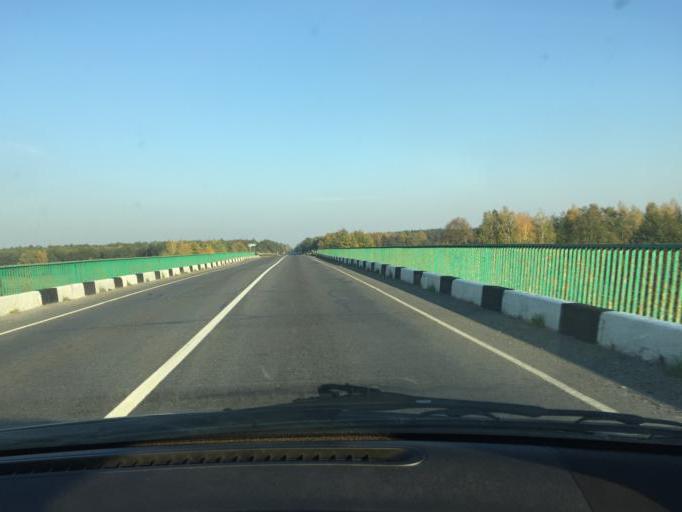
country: BY
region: Brest
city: Davyd-Haradok
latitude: 52.2360
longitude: 27.2515
